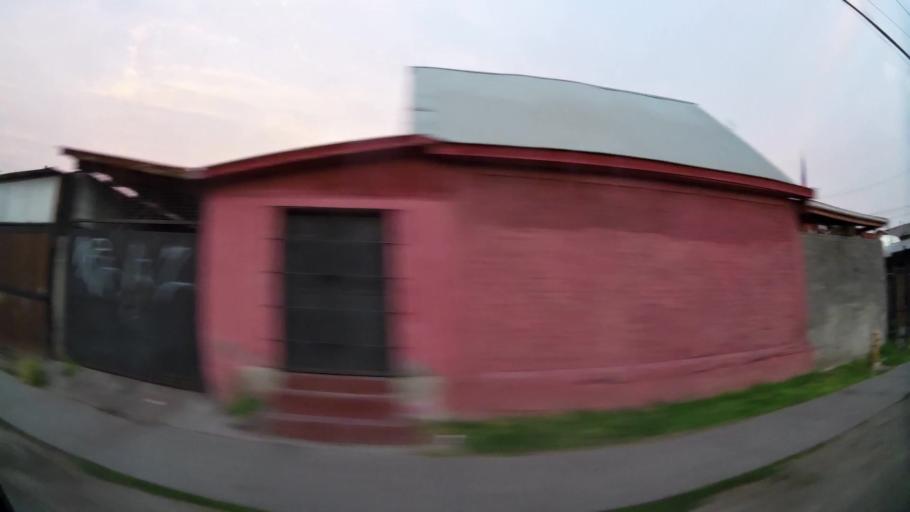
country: CL
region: Santiago Metropolitan
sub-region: Provincia de Santiago
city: Lo Prado
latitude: -33.5005
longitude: -70.7352
